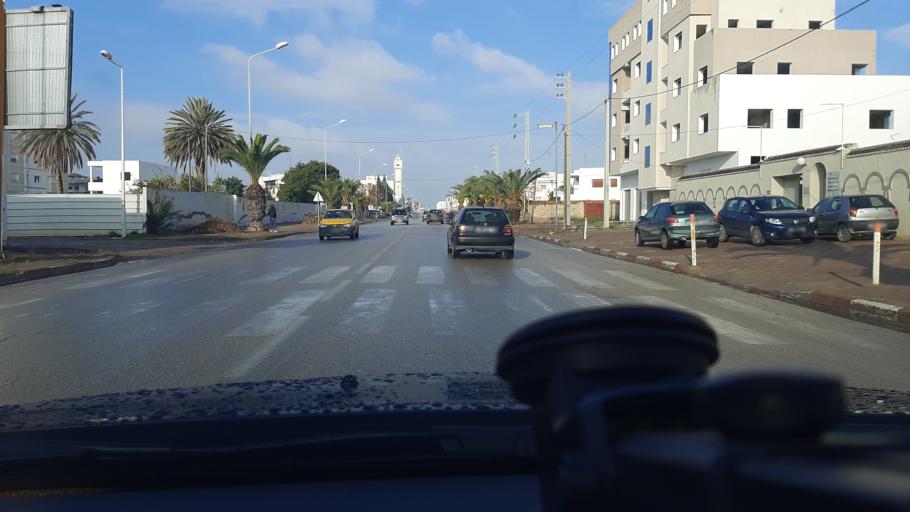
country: TN
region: Safaqis
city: Sfax
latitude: 34.7436
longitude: 10.7316
